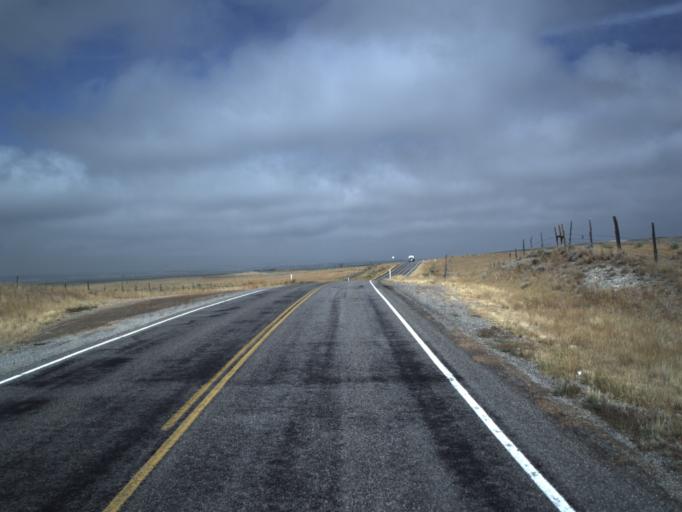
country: US
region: Utah
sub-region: Rich County
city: Randolph
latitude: 41.4600
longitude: -111.0982
